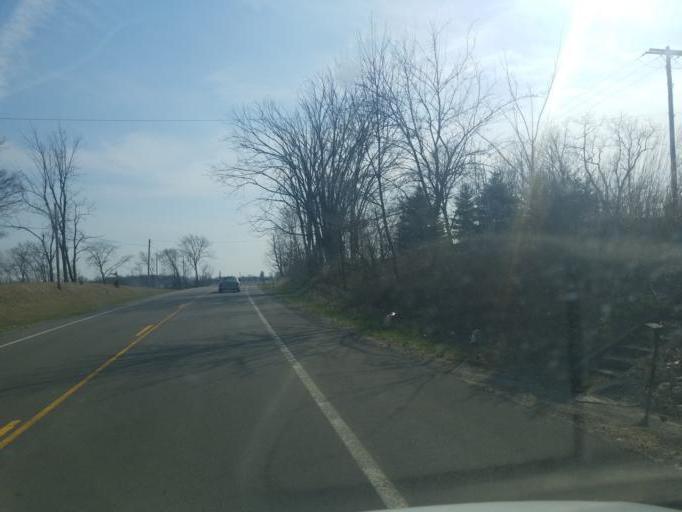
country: US
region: Ohio
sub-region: Logan County
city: Northwood
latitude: 40.4859
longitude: -83.7037
